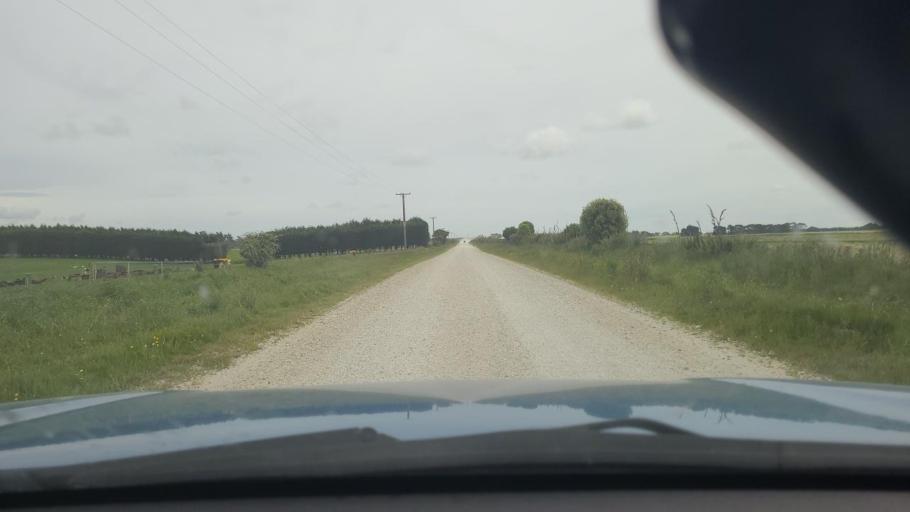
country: NZ
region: Southland
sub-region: Invercargill City
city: Invercargill
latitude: -46.5001
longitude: 168.6523
